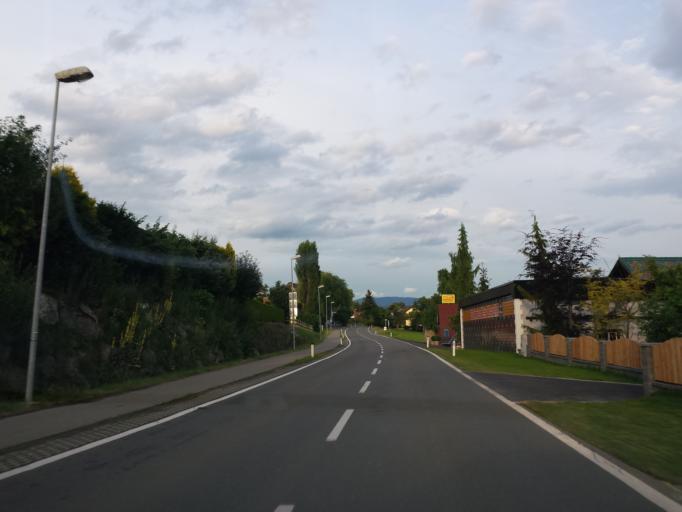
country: AT
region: Styria
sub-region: Politischer Bezirk Murtal
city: Spielberg bei Knittelfeld
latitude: 47.2146
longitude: 14.7758
